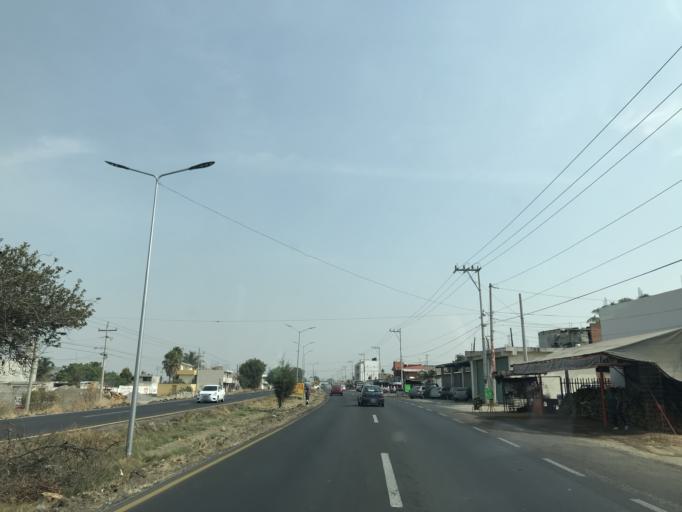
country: MX
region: Tlaxcala
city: Tenancingo
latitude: 19.1430
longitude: -98.1914
